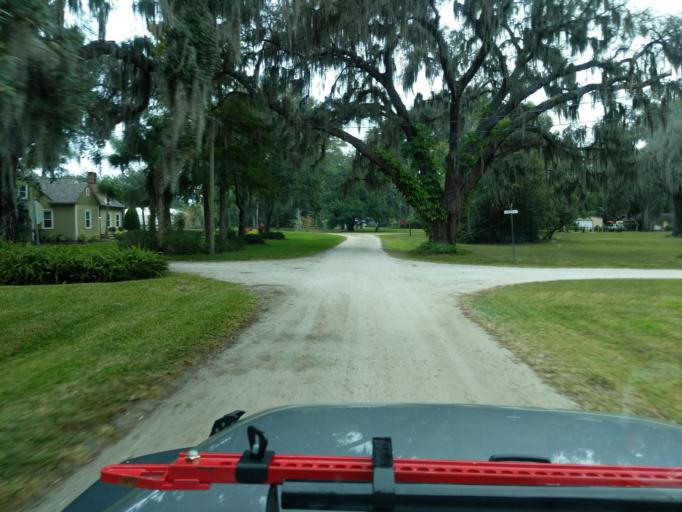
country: US
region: Florida
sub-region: Orange County
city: Oakland
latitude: 28.5559
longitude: -81.6257
